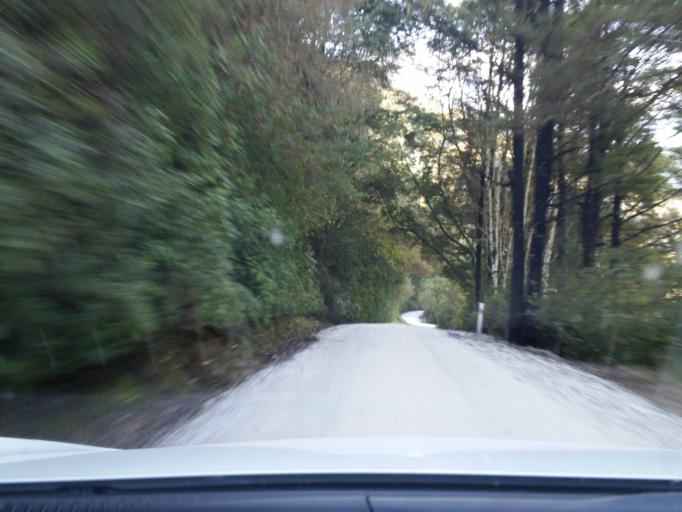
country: NZ
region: West Coast
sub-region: Buller District
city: Westport
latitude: -41.7713
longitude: 172.2277
